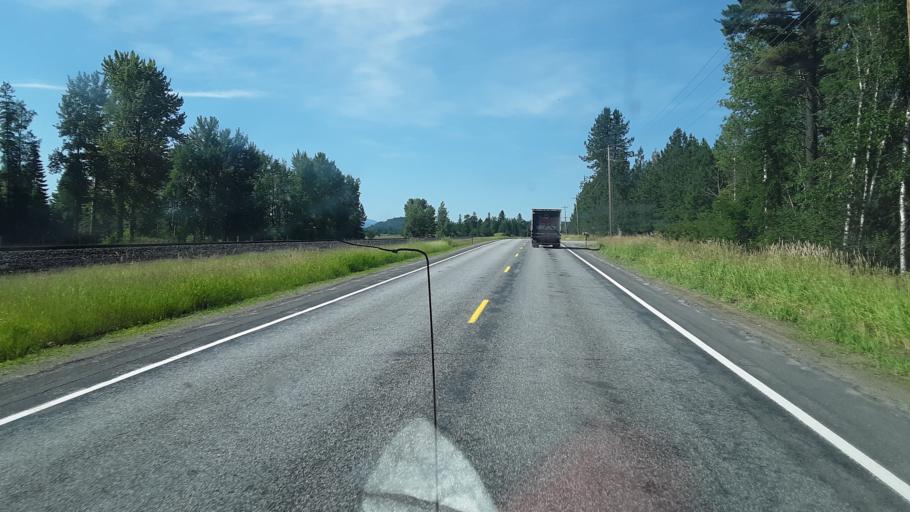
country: US
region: Idaho
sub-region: Bonner County
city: Ponderay
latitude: 48.4567
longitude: -116.4753
